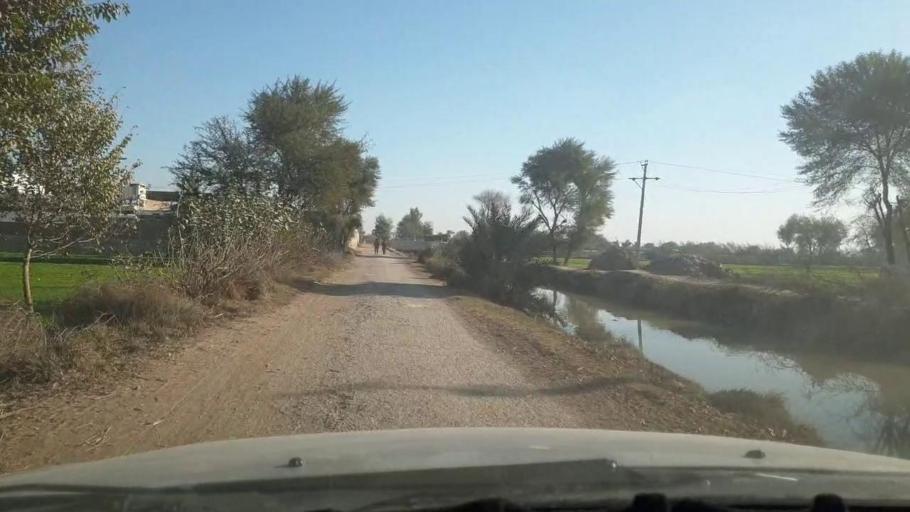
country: PK
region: Sindh
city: Adilpur
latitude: 27.9413
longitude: 69.2205
